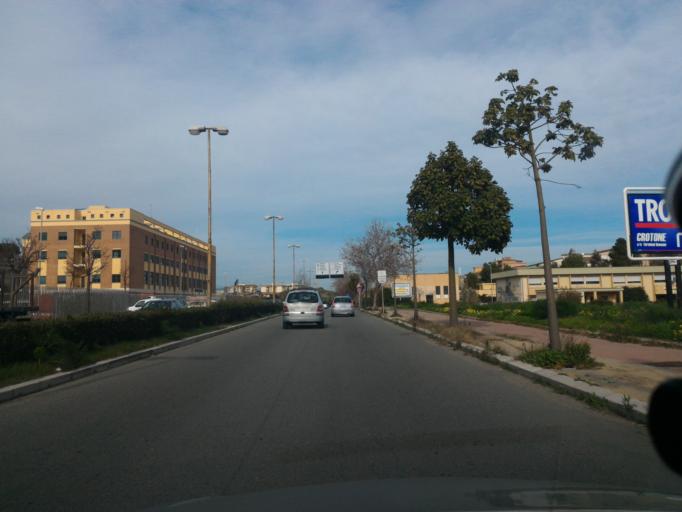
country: IT
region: Calabria
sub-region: Provincia di Crotone
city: Crotone
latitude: 39.0706
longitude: 17.1136
